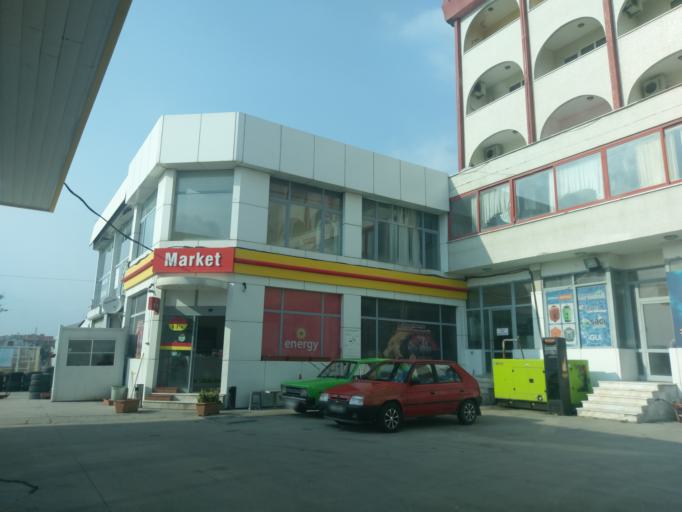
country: TR
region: Istanbul
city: Selimpasa
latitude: 41.0518
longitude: 28.3871
